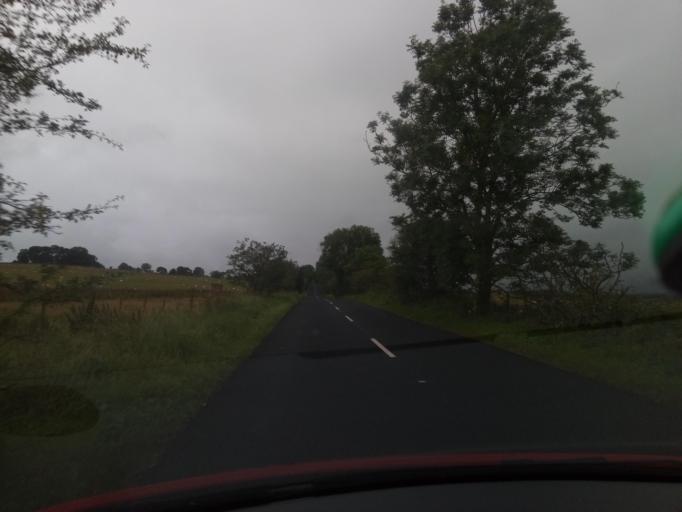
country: GB
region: England
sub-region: Northumberland
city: Rothley
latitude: 55.2002
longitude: -1.9621
